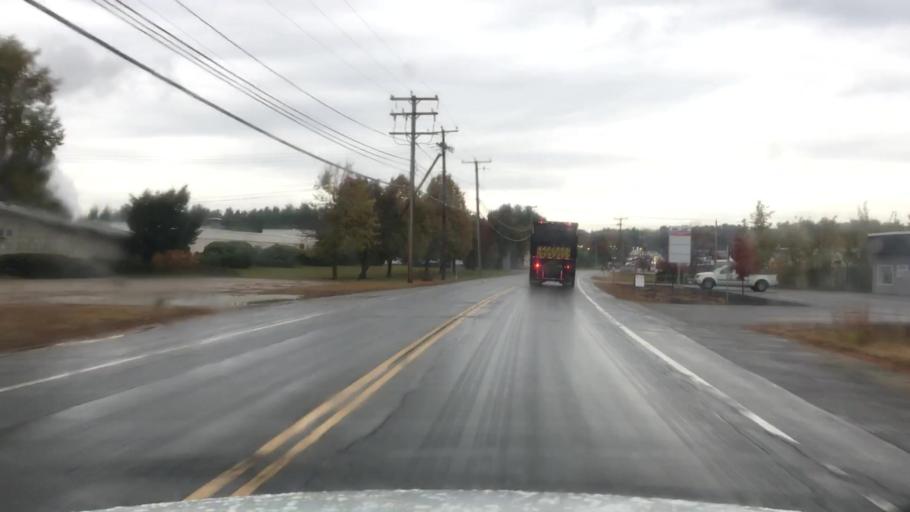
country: US
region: New Hampshire
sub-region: Strafford County
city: Somersworth
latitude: 43.2601
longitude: -70.9041
